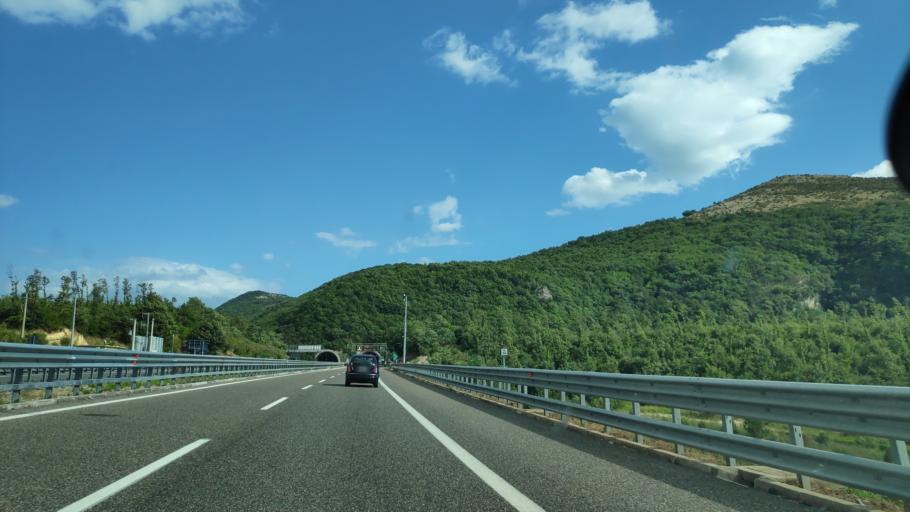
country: IT
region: Campania
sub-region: Provincia di Salerno
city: Sicignano degli Alburni
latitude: 40.6078
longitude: 15.2976
